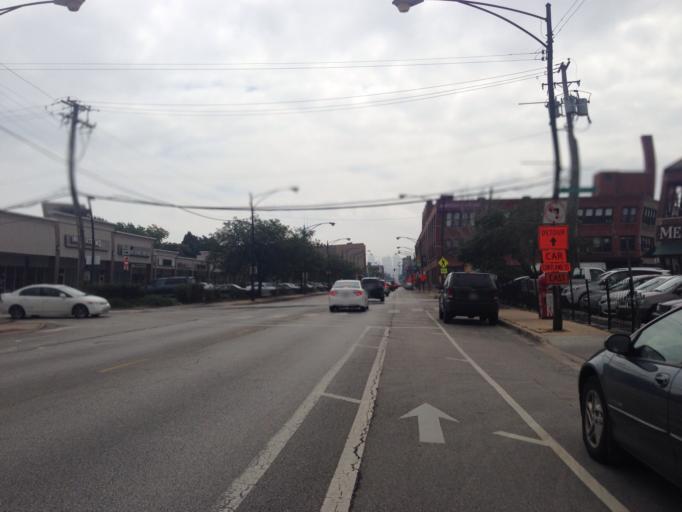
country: US
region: Illinois
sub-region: Cook County
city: Chicago
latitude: 41.9196
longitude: -87.6617
